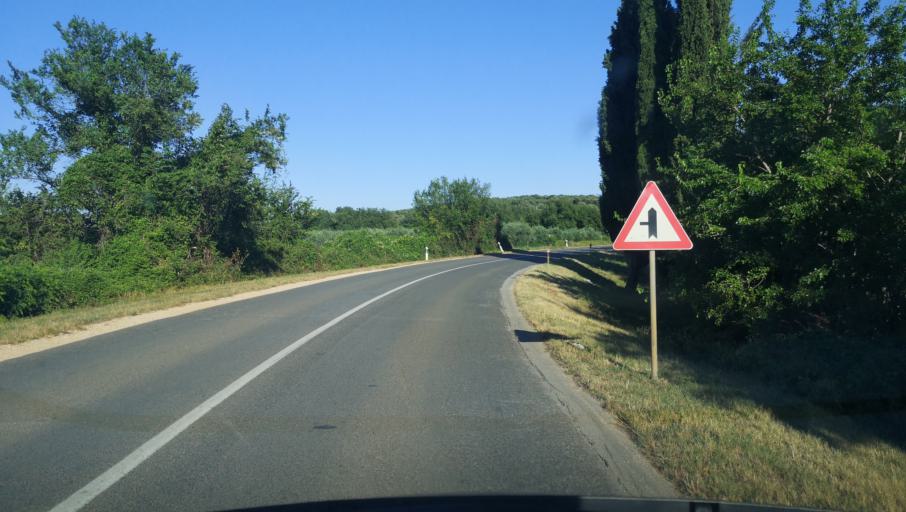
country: HR
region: Istarska
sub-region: Grad Rovinj
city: Rovinj
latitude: 45.0809
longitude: 13.6726
